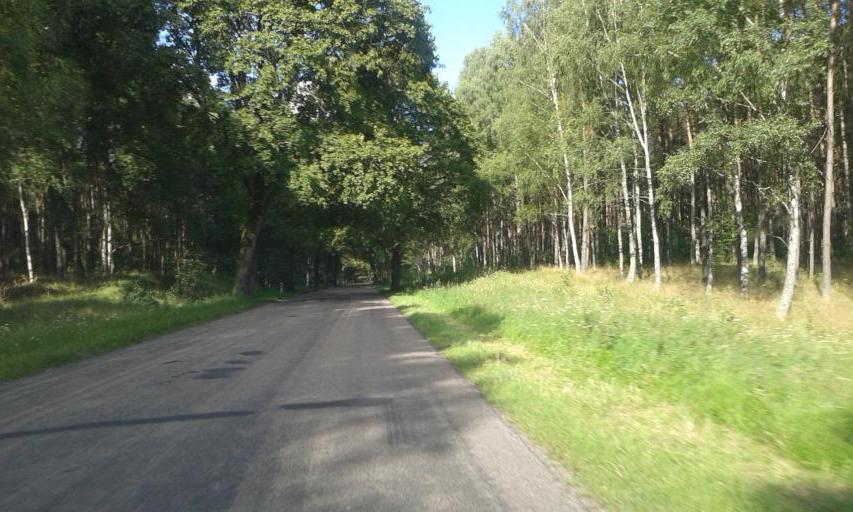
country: PL
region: West Pomeranian Voivodeship
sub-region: Powiat szczecinecki
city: Barwice
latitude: 53.6566
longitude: 16.3232
